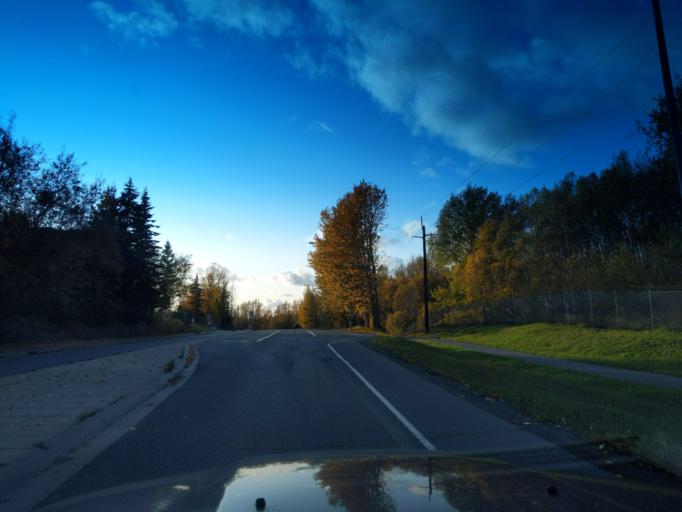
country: US
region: Alaska
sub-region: Anchorage Municipality
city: Anchorage
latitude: 61.1665
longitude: -149.9450
